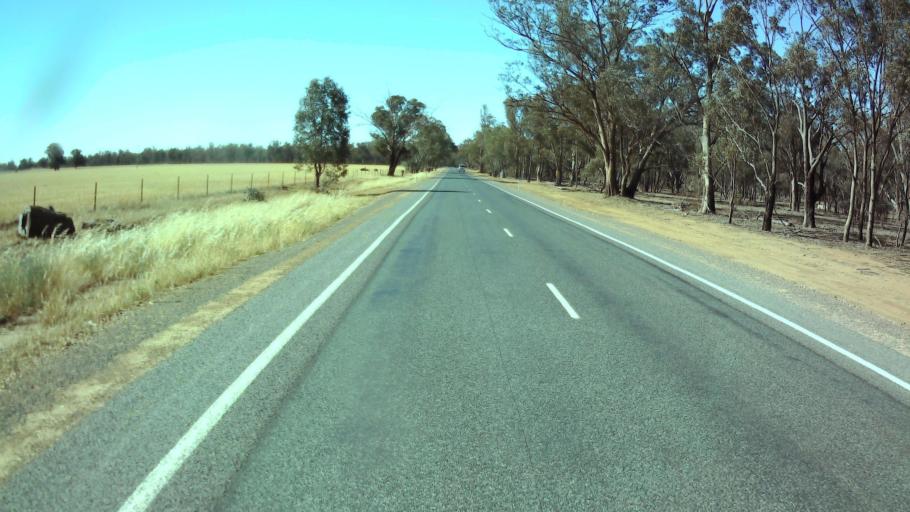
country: AU
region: New South Wales
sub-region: Weddin
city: Grenfell
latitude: -33.7354
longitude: 148.0887
